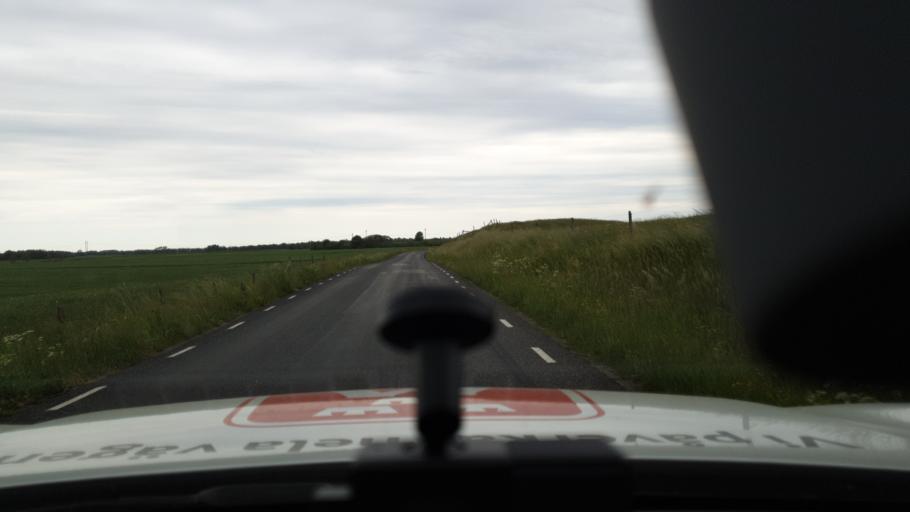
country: SE
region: Vaestra Goetaland
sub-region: Falkopings Kommun
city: Falkoeping
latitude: 58.0945
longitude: 13.5005
